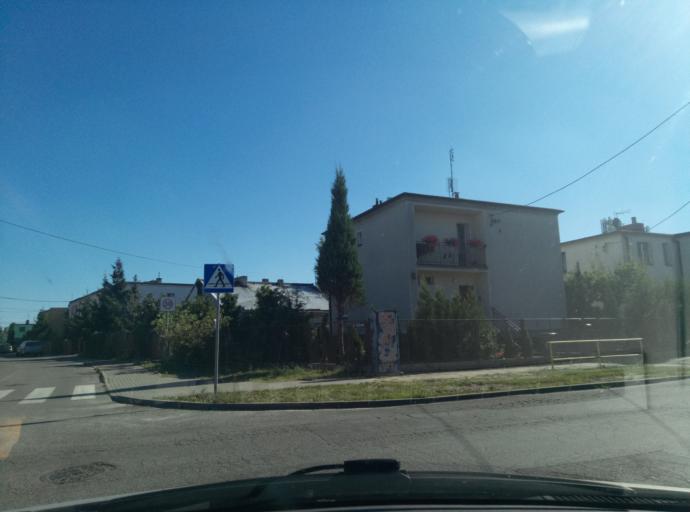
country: PL
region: Kujawsko-Pomorskie
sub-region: Torun
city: Torun
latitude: 53.0469
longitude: 18.5801
